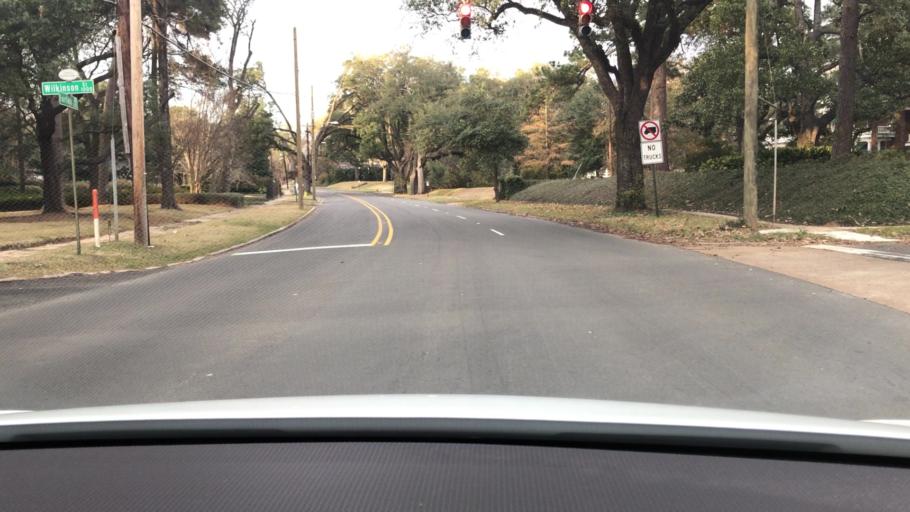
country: US
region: Louisiana
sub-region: Bossier Parish
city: Bossier City
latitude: 32.4853
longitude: -93.7497
